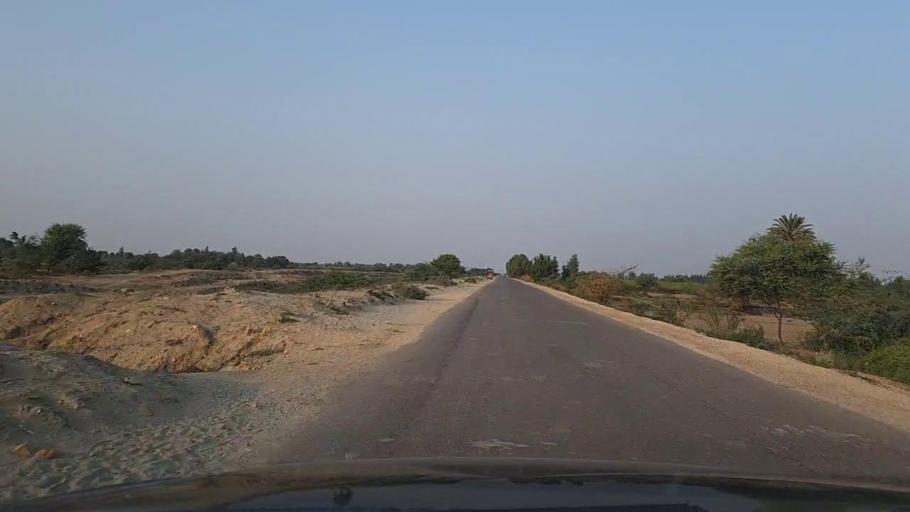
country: PK
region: Sindh
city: Mirpur Sakro
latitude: 24.4949
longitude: 67.8114
